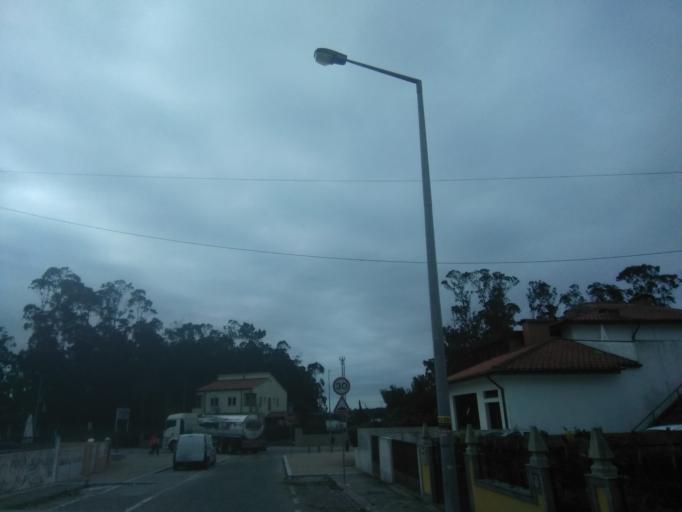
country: PT
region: Porto
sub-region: Matosinhos
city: Lavra
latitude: 41.2782
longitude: -8.7196
